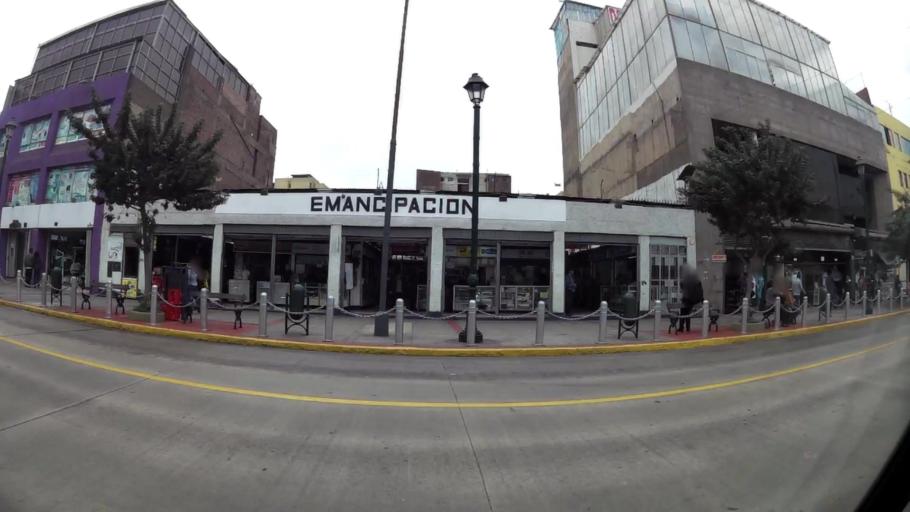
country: PE
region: Lima
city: Lima
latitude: -12.0474
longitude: -77.0359
